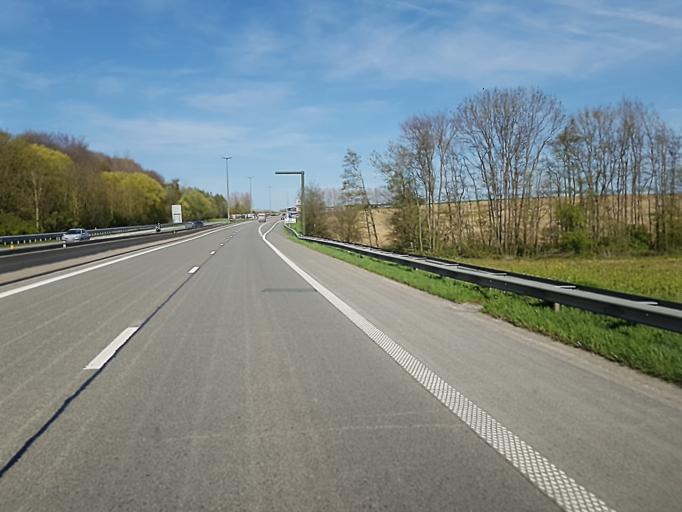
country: BE
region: Wallonia
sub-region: Province du Hainaut
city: Silly
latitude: 50.6799
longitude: 3.8910
